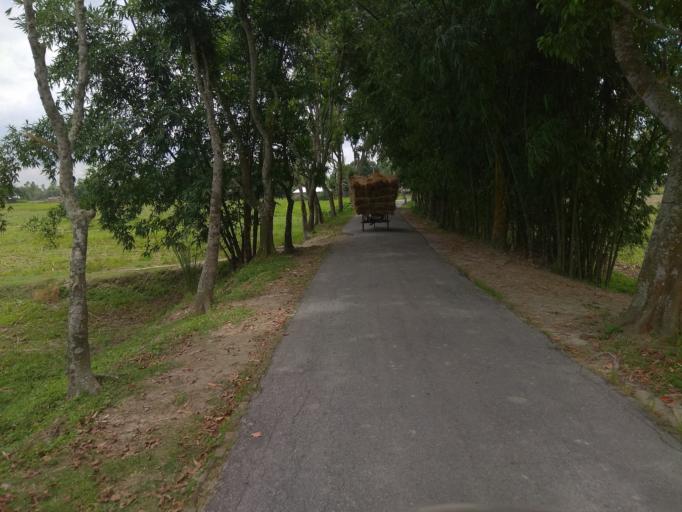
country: IN
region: West Bengal
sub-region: Koch Bihar
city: Haldibari
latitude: 26.2425
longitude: 88.8923
